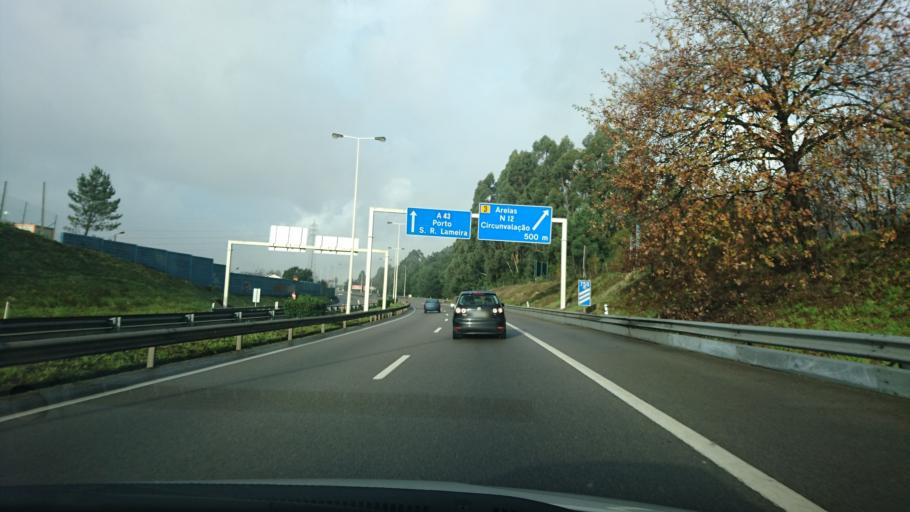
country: PT
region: Porto
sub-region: Gondomar
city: Gondomar
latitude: 41.1541
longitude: -8.5512
